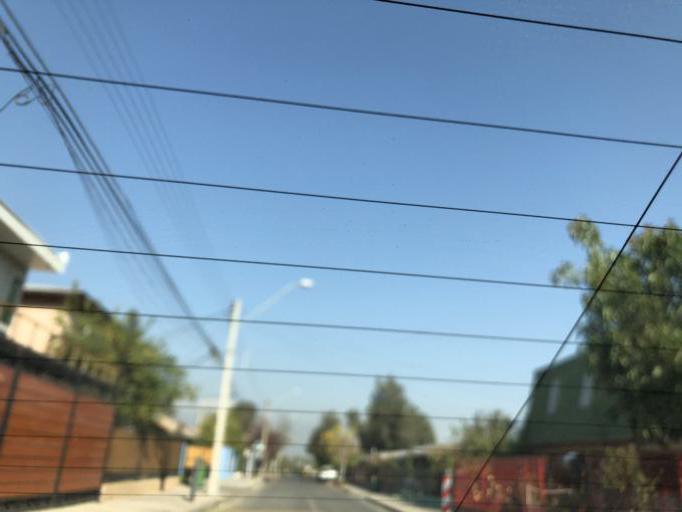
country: CL
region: Santiago Metropolitan
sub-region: Provincia de Cordillera
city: Puente Alto
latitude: -33.6119
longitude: -70.5591
